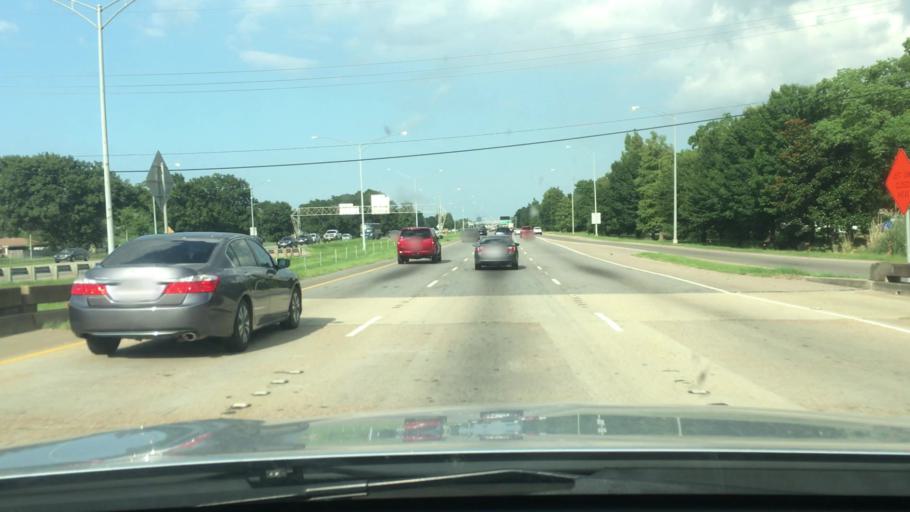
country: US
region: Louisiana
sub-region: Jefferson Parish
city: Kenner
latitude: 30.0078
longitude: -90.2636
